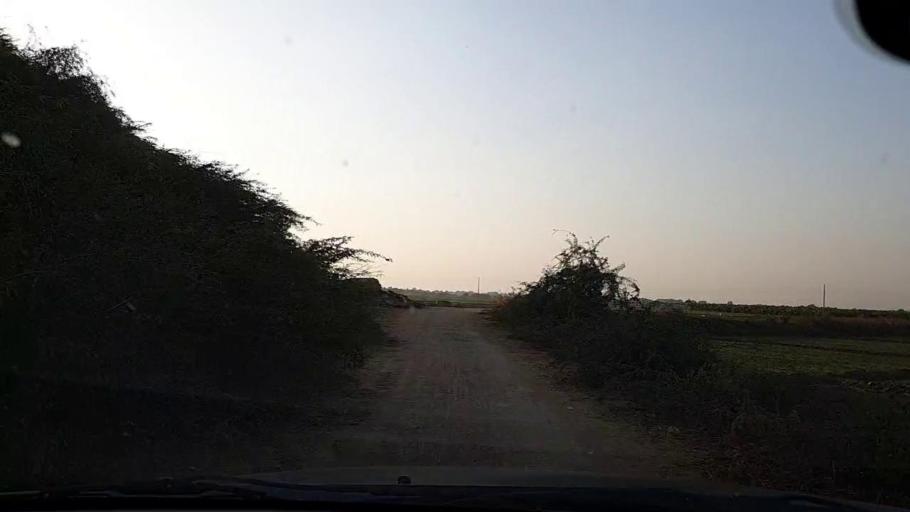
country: PK
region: Sindh
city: Thatta
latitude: 24.5626
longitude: 67.8798
